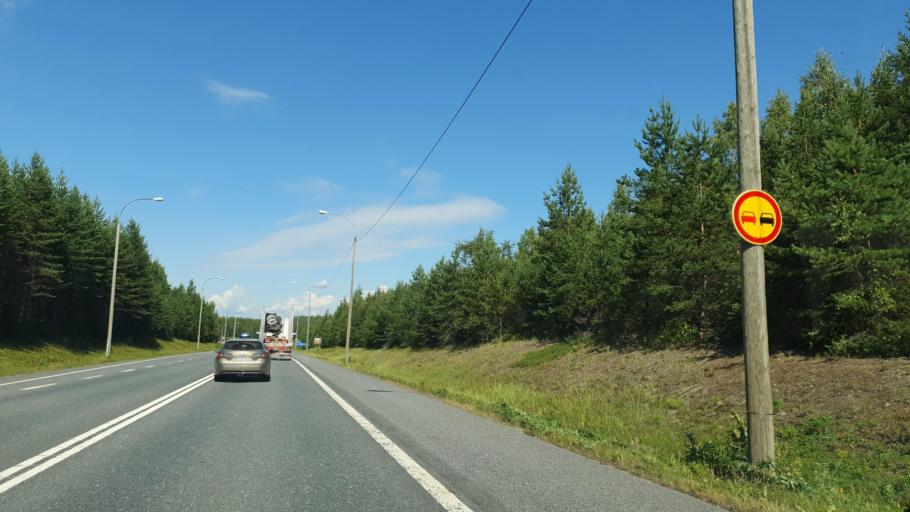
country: FI
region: Northern Savo
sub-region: Ylae-Savo
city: Iisalmi
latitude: 63.5853
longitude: 27.2301
